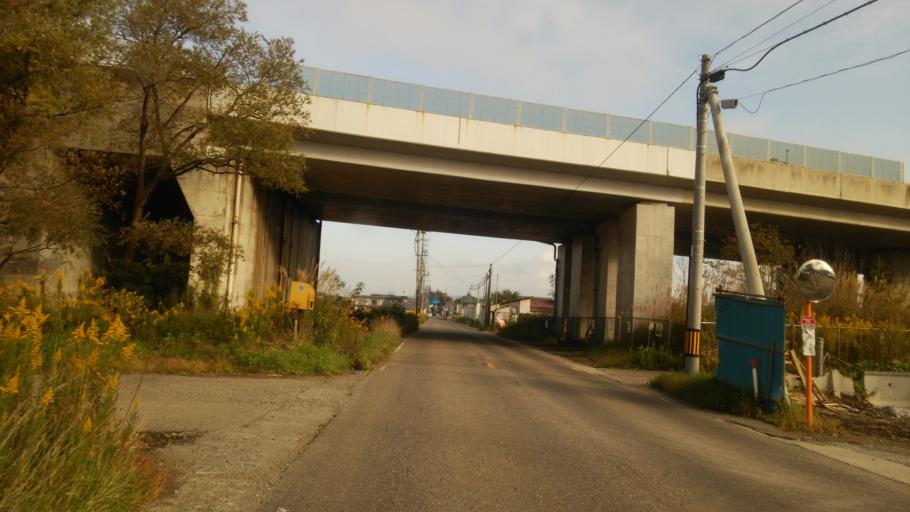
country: JP
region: Fukushima
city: Kitakata
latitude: 37.5258
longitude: 139.9314
